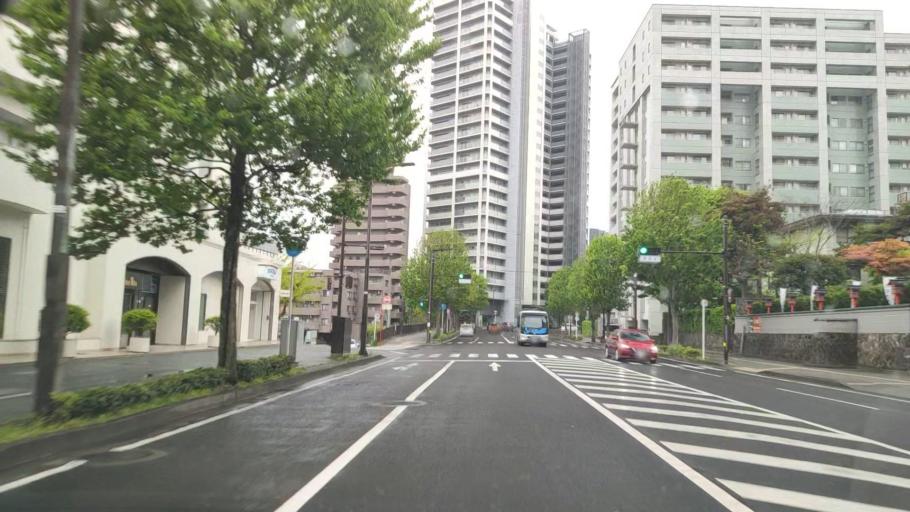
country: JP
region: Miyagi
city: Sendai
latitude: 38.2577
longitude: 140.8659
